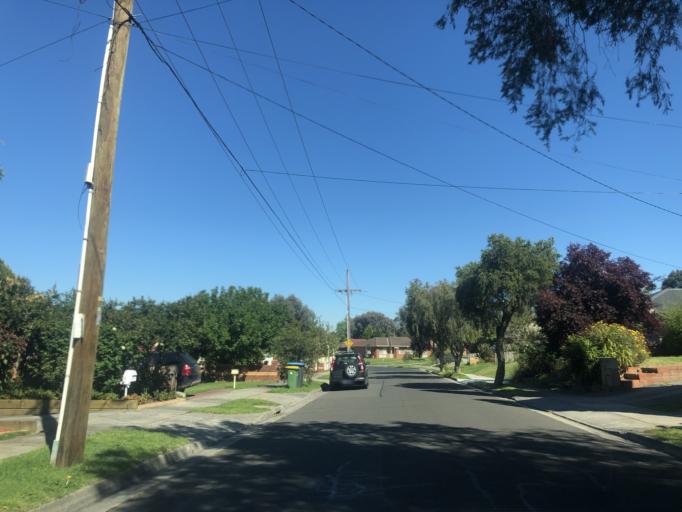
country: AU
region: Victoria
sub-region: Knox
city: Rowville
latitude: -37.9223
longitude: 145.2289
